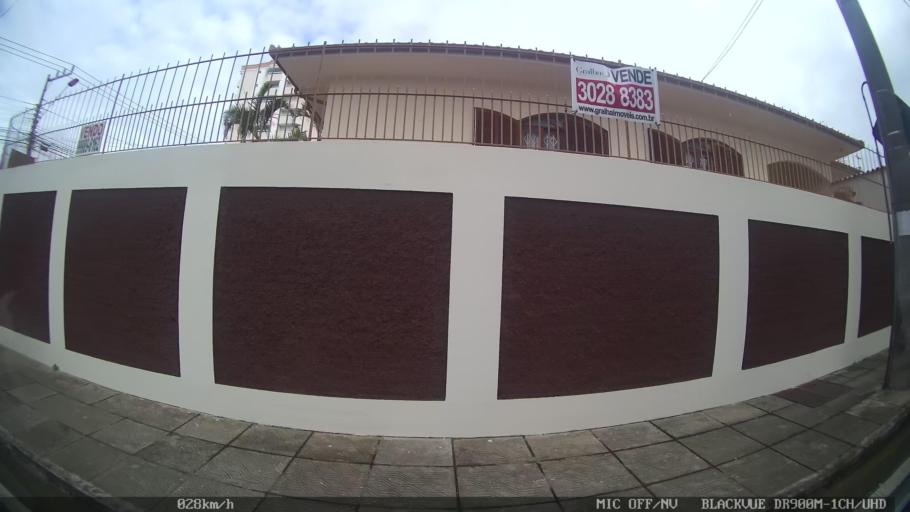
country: BR
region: Santa Catarina
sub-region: Sao Jose
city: Campinas
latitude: -27.5779
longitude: -48.6072
